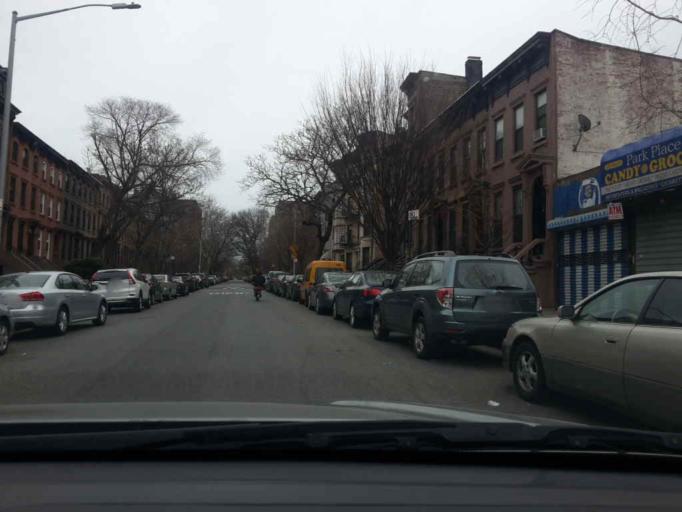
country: US
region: New York
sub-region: Kings County
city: Brooklyn
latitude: 40.6774
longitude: -73.9721
